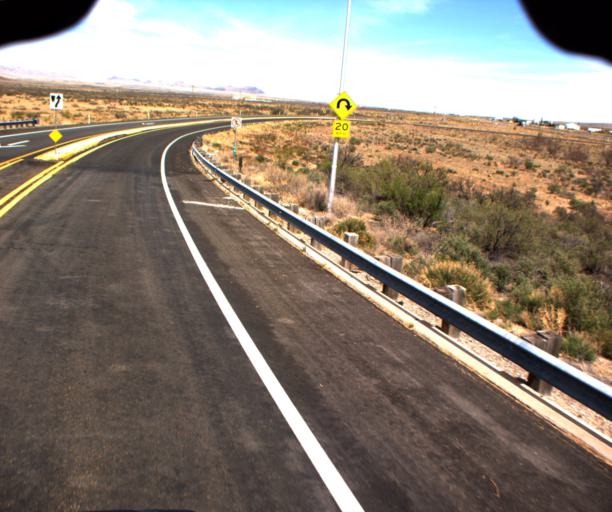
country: US
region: Arizona
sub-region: Cochise County
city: Willcox
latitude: 32.3092
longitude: -109.7965
